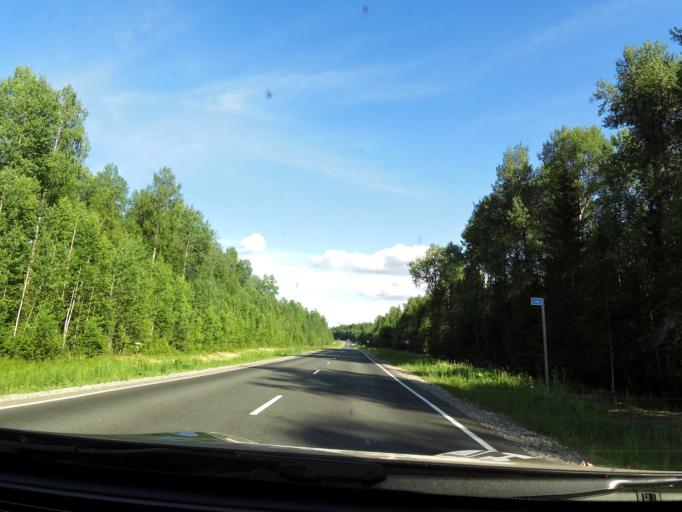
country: RU
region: Kirov
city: Chernaya Kholunitsa
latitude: 58.7799
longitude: 51.9161
